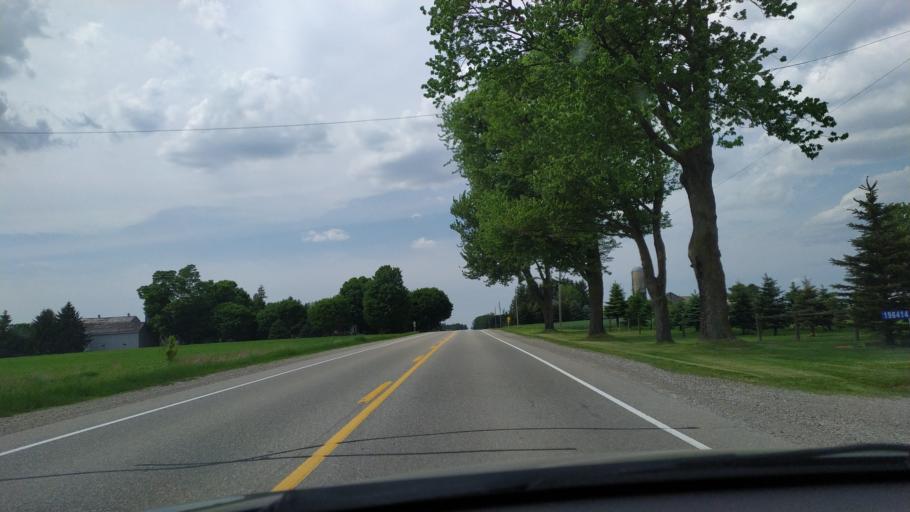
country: CA
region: Ontario
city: Dorchester
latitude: 43.1782
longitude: -81.0501
